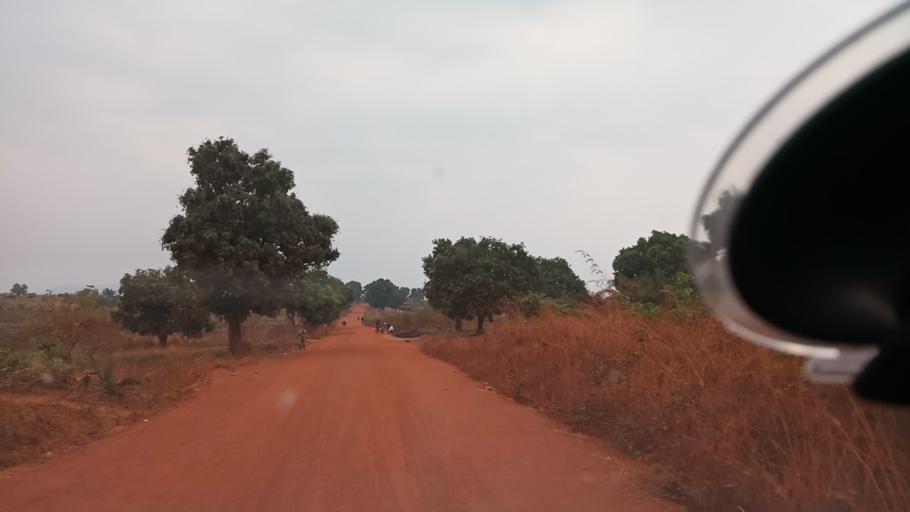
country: ZM
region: Luapula
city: Nchelenge
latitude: -9.1804
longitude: 28.2826
